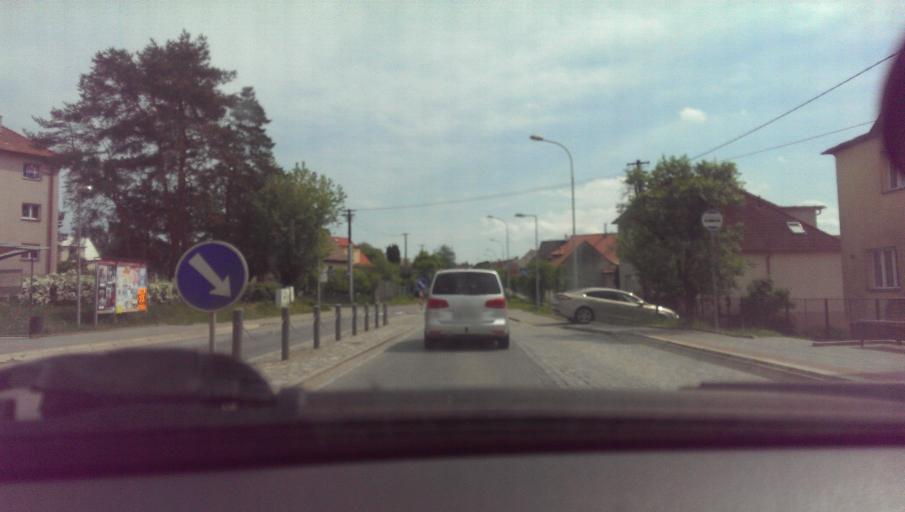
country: CZ
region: Zlin
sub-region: Okres Zlin
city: Napajedla
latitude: 49.1652
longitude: 17.5147
